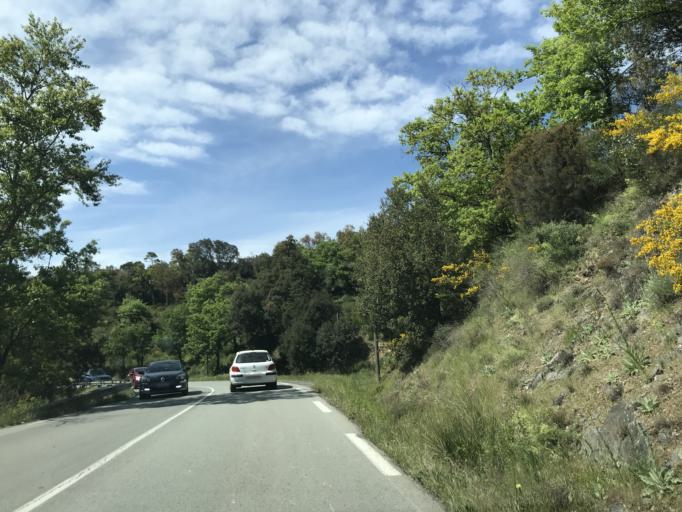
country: FR
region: Provence-Alpes-Cote d'Azur
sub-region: Departement du Var
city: Montauroux
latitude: 43.5861
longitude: 6.7945
